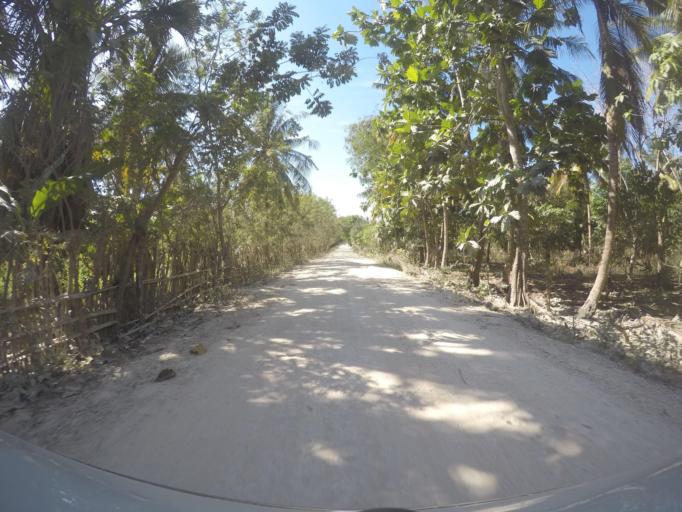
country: TL
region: Viqueque
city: Viqueque
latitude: -8.8854
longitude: 126.5071
